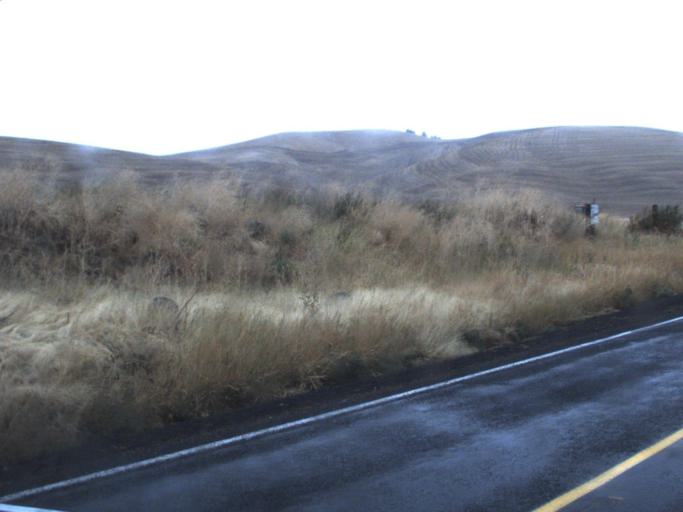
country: US
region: Washington
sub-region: Whitman County
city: Colfax
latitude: 47.0265
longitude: -117.4957
